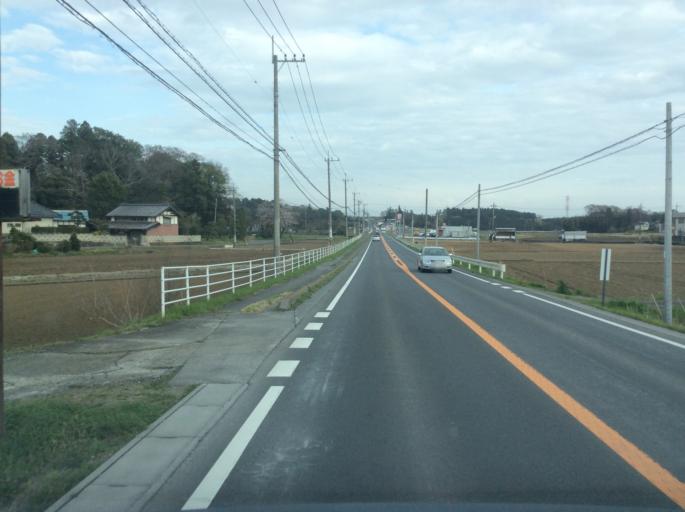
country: JP
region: Ibaraki
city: Tsukuba
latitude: 36.1850
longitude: 140.0316
